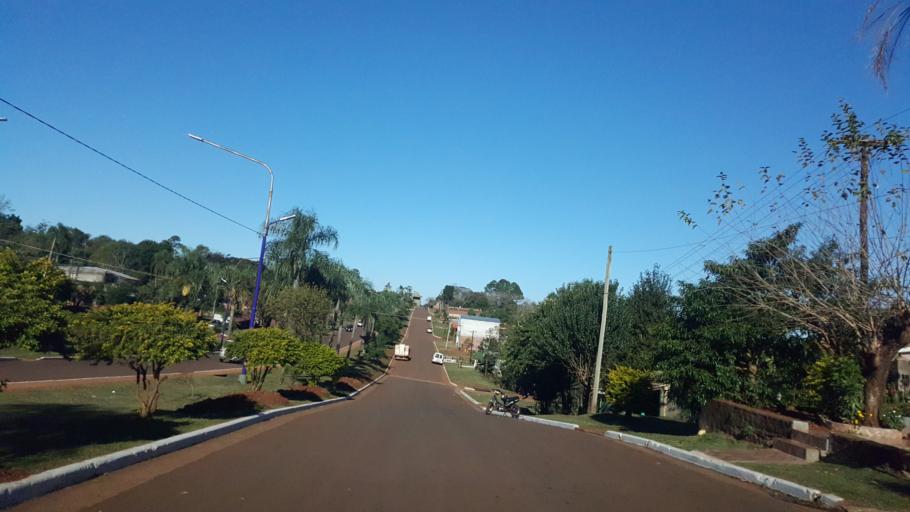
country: AR
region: Misiones
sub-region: Departamento de San Ignacio
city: San Ignacio
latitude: -27.2579
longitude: -55.5351
